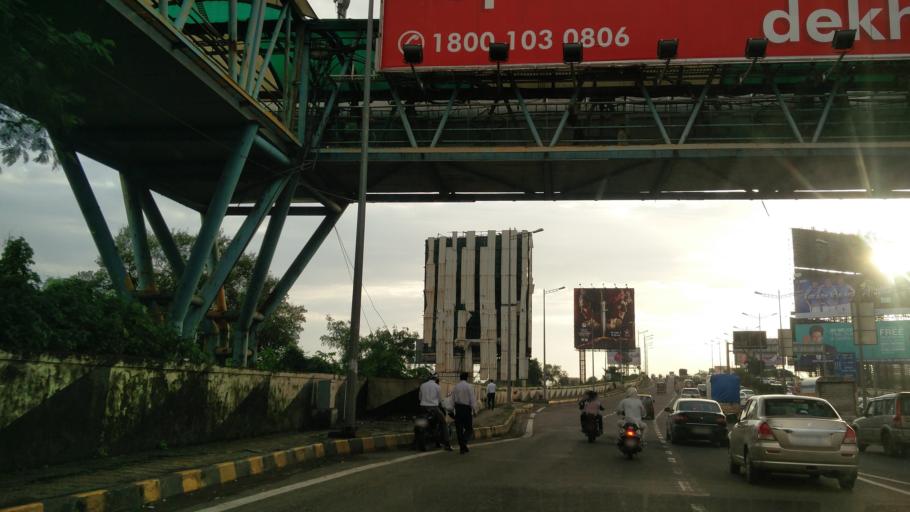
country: IN
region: Maharashtra
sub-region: Mumbai Suburban
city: Mumbai
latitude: 19.0526
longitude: 72.8452
